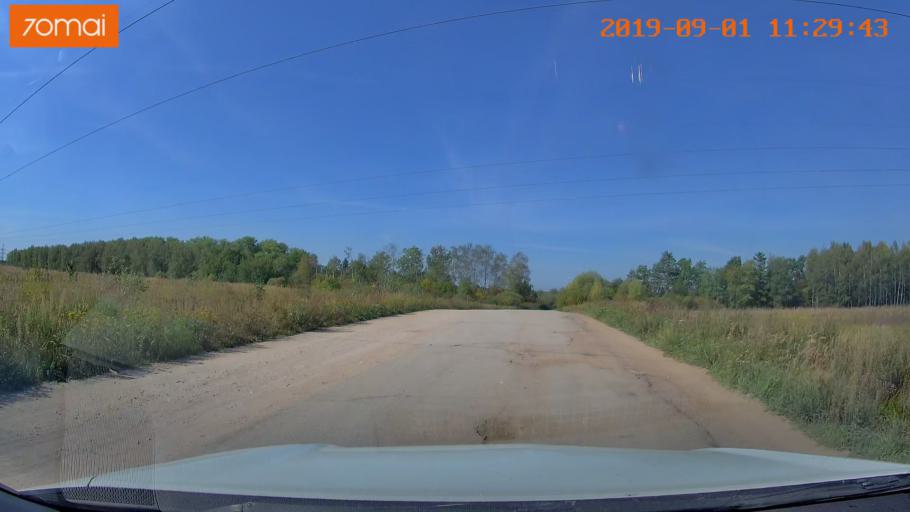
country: RU
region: Kaluga
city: Detchino
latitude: 54.8338
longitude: 36.3443
